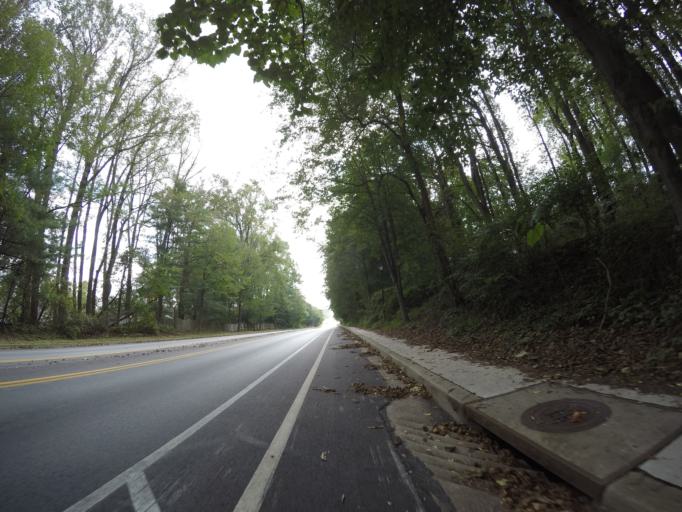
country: US
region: Maryland
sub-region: Howard County
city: Columbia
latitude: 39.2616
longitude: -76.8632
